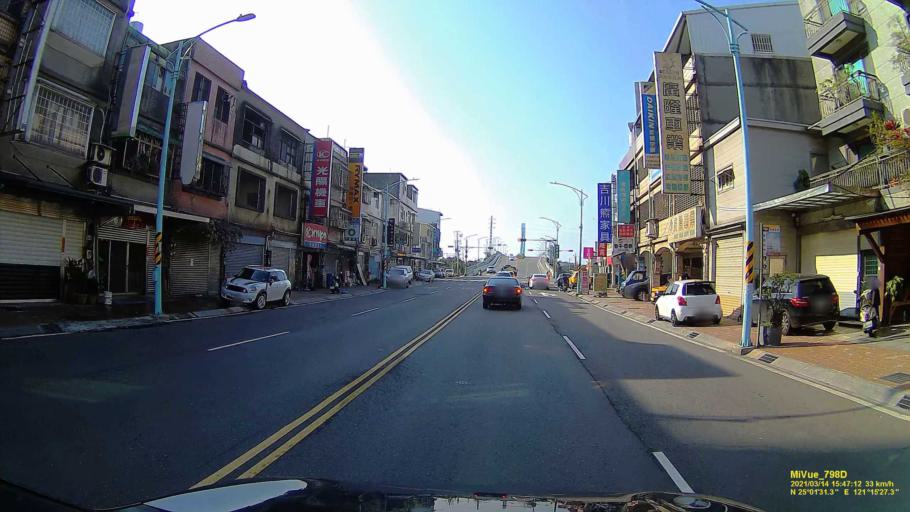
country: TW
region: Taiwan
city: Taoyuan City
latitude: 25.0255
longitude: 121.2575
